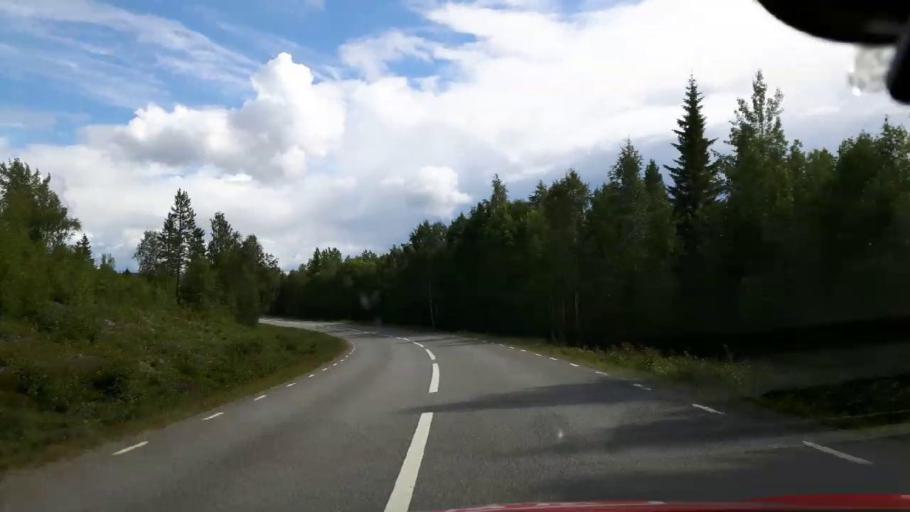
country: SE
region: Jaemtland
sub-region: Stroemsunds Kommun
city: Stroemsund
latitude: 64.3423
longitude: 15.1104
